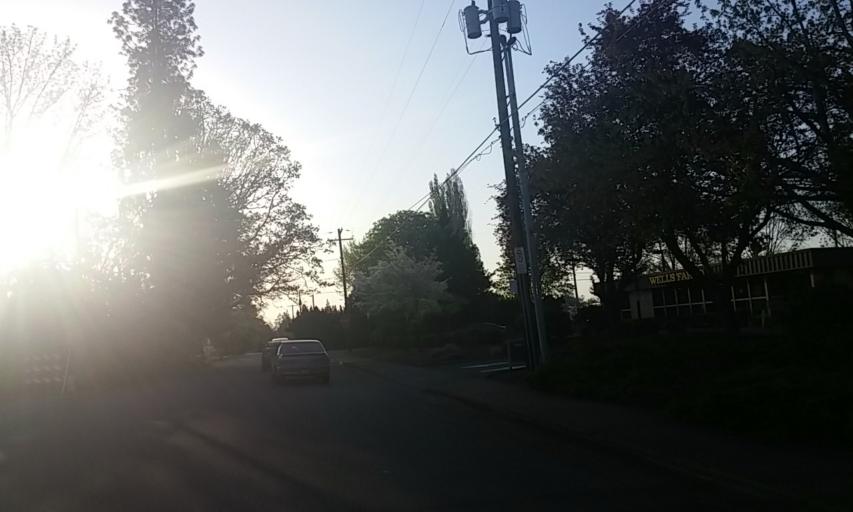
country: US
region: Oregon
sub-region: Washington County
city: Aloha
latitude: 45.4950
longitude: -122.8652
